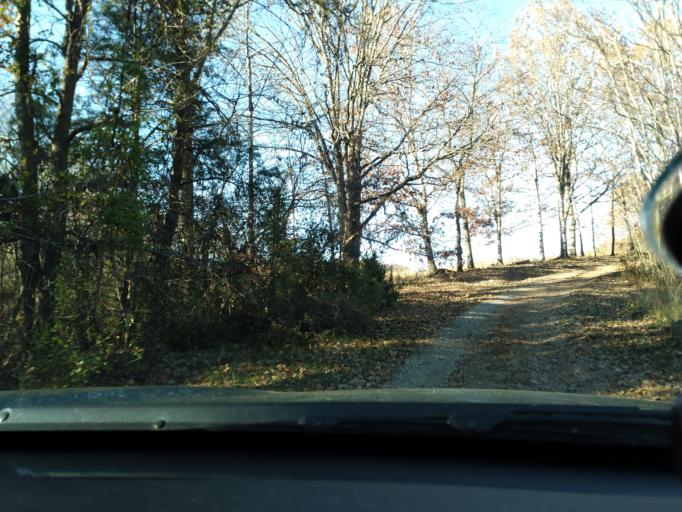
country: US
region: Virginia
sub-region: Floyd County
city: Floyd
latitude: 36.8352
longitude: -80.1844
